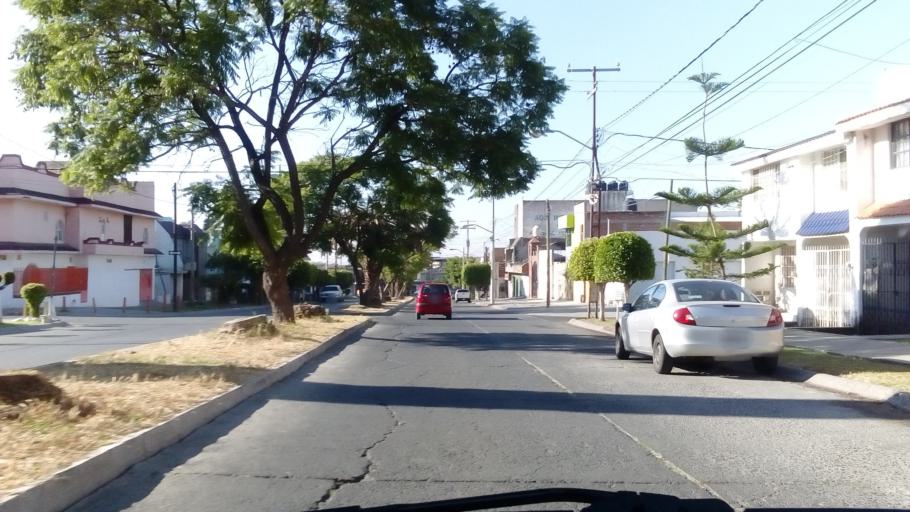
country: MX
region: Guanajuato
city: Leon
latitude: 21.1157
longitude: -101.6997
